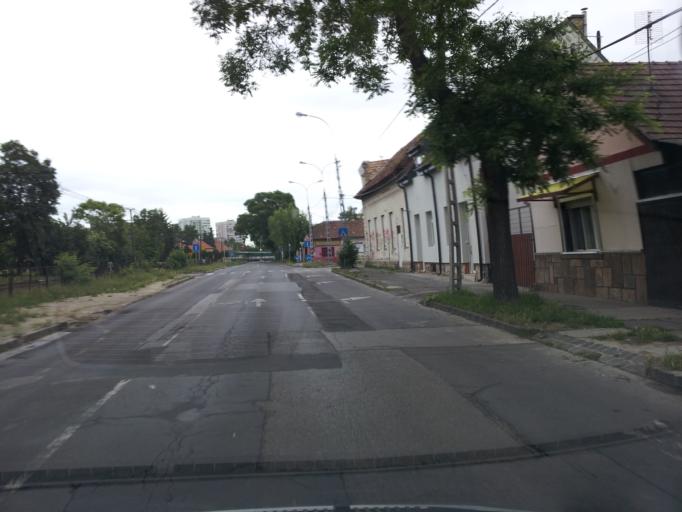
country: HU
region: Pest
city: Budakalasz
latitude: 47.5897
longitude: 19.0479
